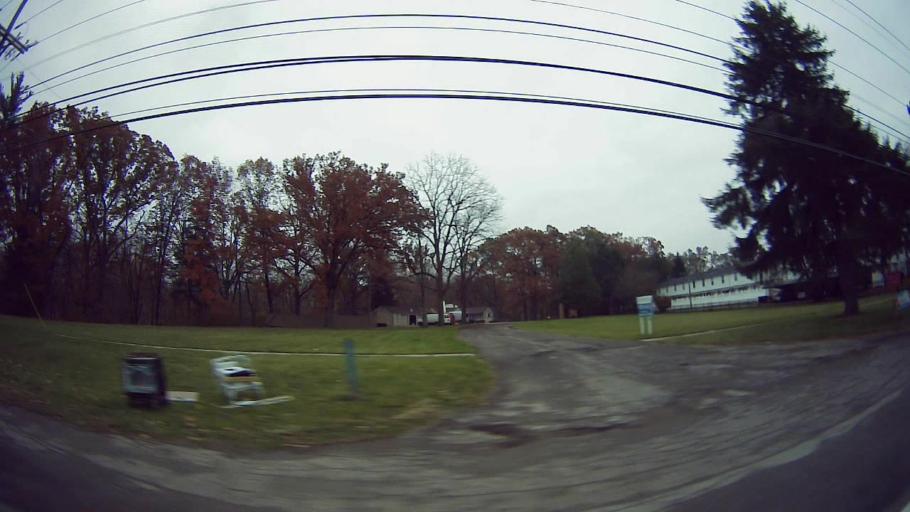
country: US
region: Michigan
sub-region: Oakland County
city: Southfield
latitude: 42.4674
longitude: -83.2605
